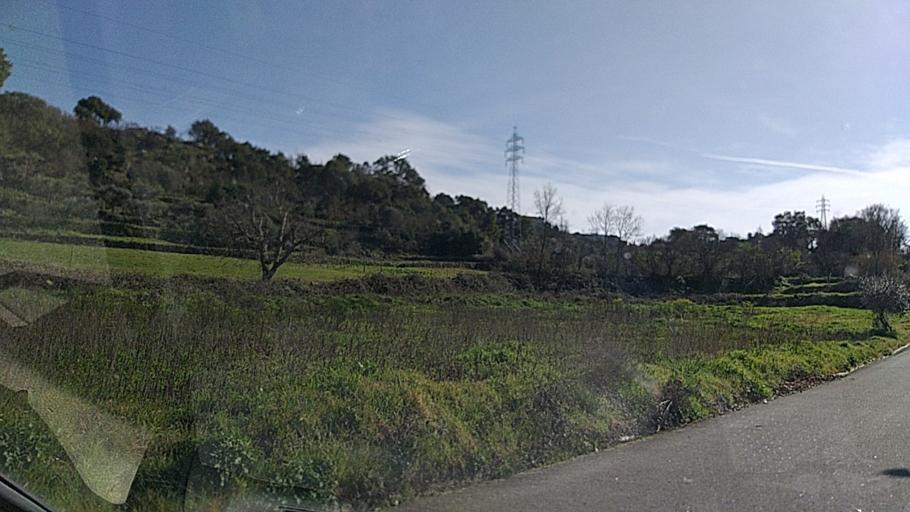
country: PT
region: Guarda
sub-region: Celorico da Beira
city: Celorico da Beira
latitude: 40.6381
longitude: -7.3969
